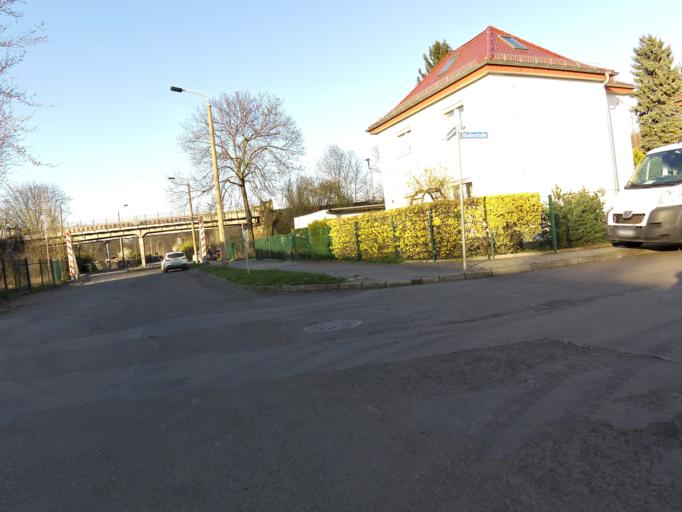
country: DE
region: Saxony
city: Markkleeberg
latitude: 51.3050
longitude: 12.3327
